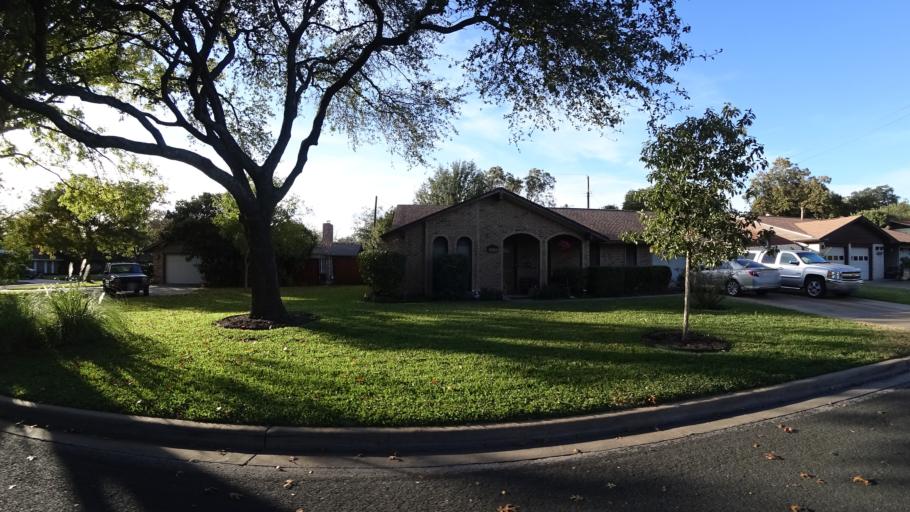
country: US
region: Texas
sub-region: Williamson County
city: Jollyville
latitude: 30.3710
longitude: -97.7317
